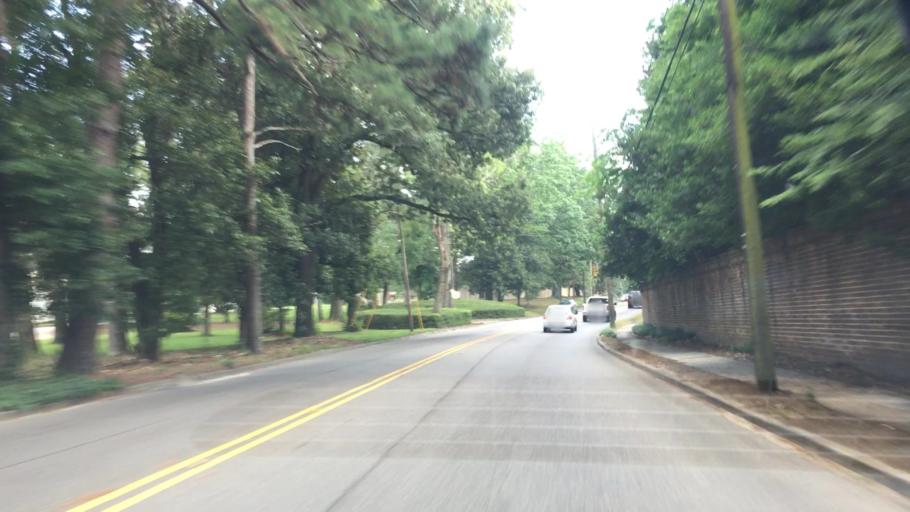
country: US
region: South Carolina
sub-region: Aiken County
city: Aiken
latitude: 33.5461
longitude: -81.7212
